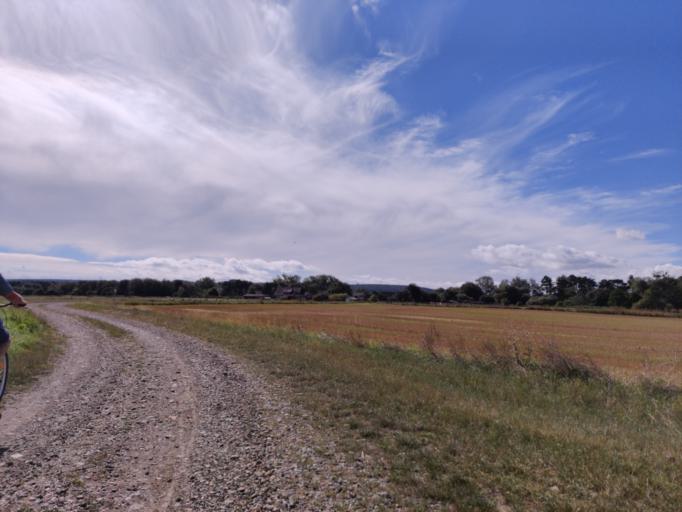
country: DE
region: Lower Saxony
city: Sehlde
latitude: 52.0424
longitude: 10.2781
